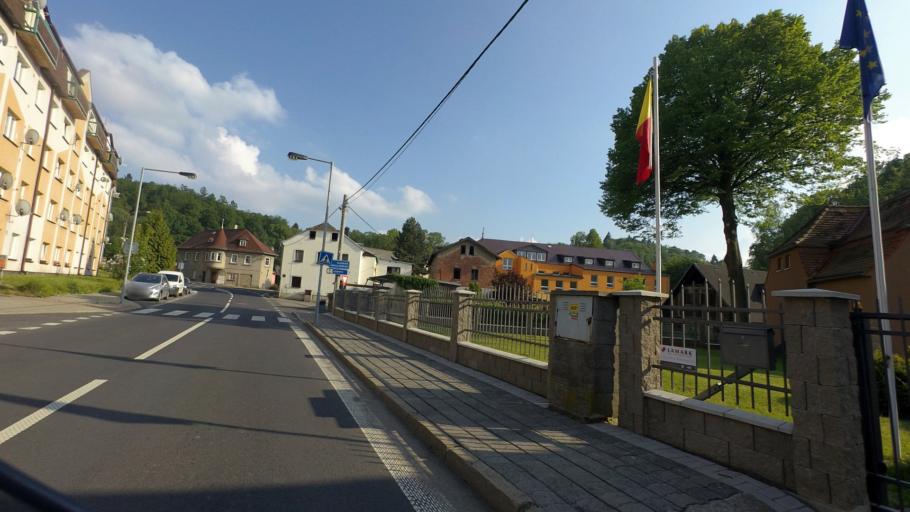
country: CZ
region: Ustecky
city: Dolni Poustevna
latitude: 50.9794
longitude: 14.2885
